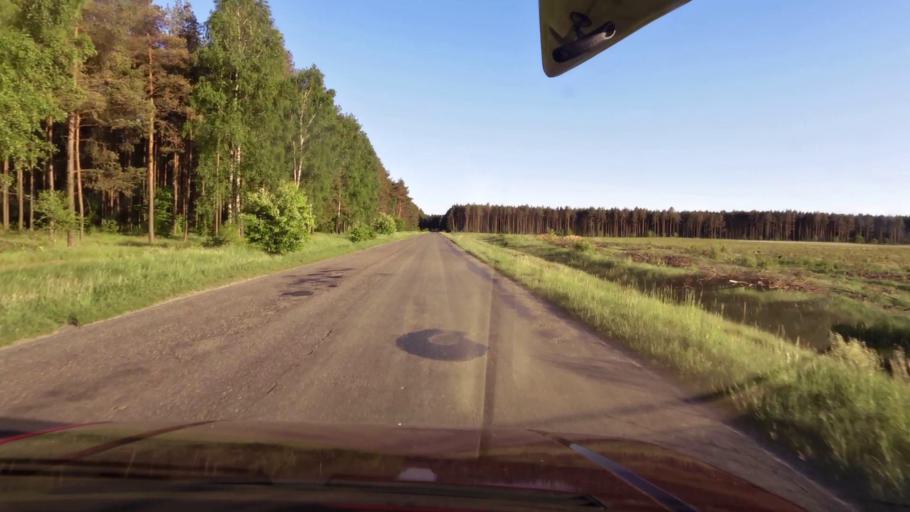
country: PL
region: West Pomeranian Voivodeship
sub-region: Powiat szczecinecki
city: Bialy Bor
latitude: 53.9053
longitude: 16.8121
